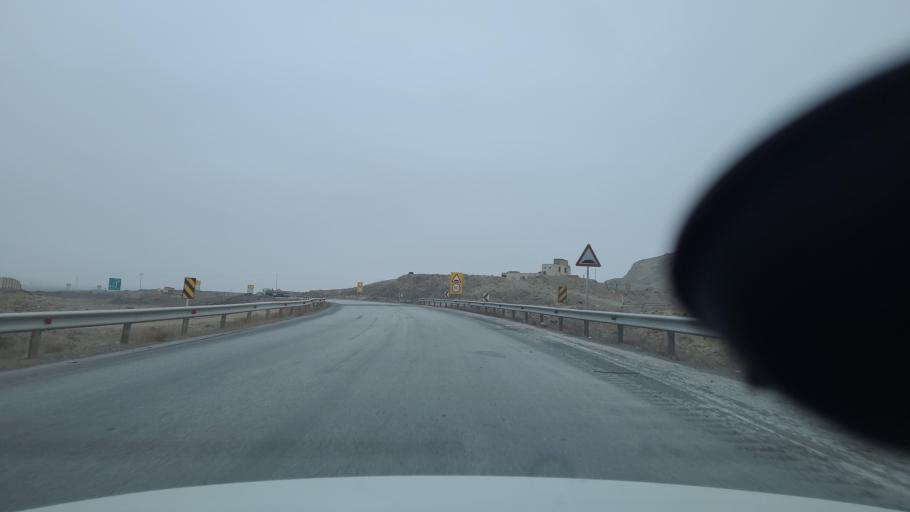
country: IR
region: Razavi Khorasan
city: Fariman
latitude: 35.9890
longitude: 59.7410
